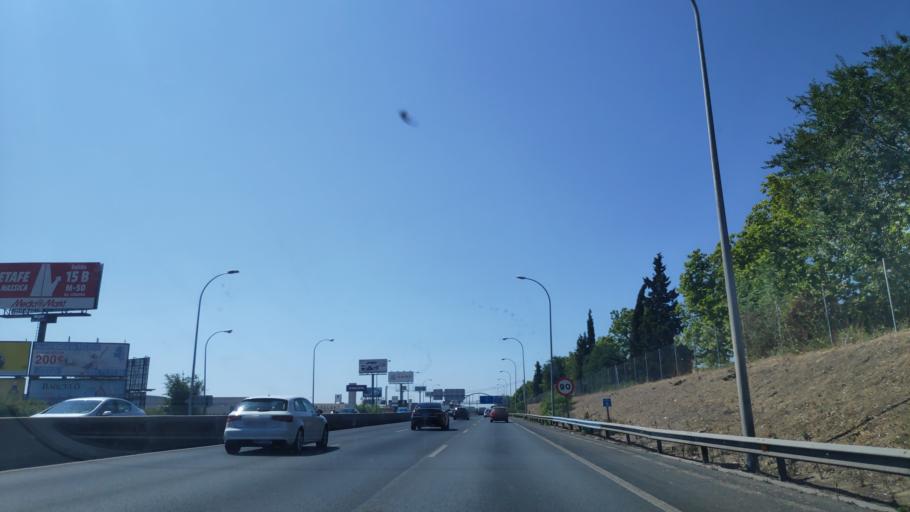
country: ES
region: Madrid
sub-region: Provincia de Madrid
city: Getafe
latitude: 40.2945
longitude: -3.7384
